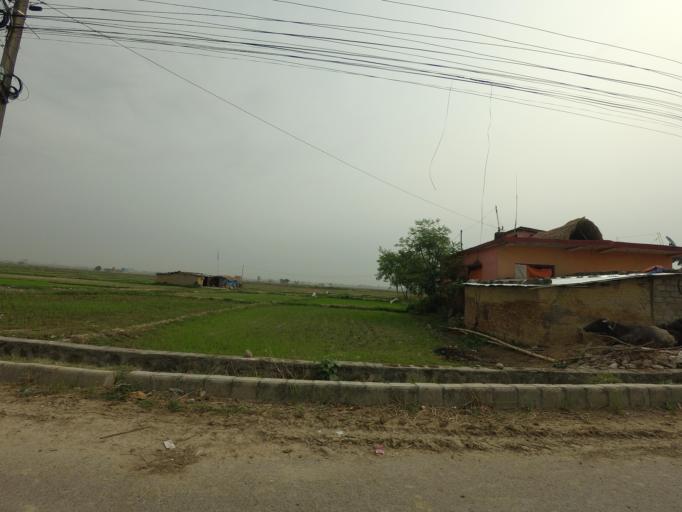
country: NP
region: Western Region
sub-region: Lumbini Zone
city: Bhairahawa
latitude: 27.4891
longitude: 83.4337
